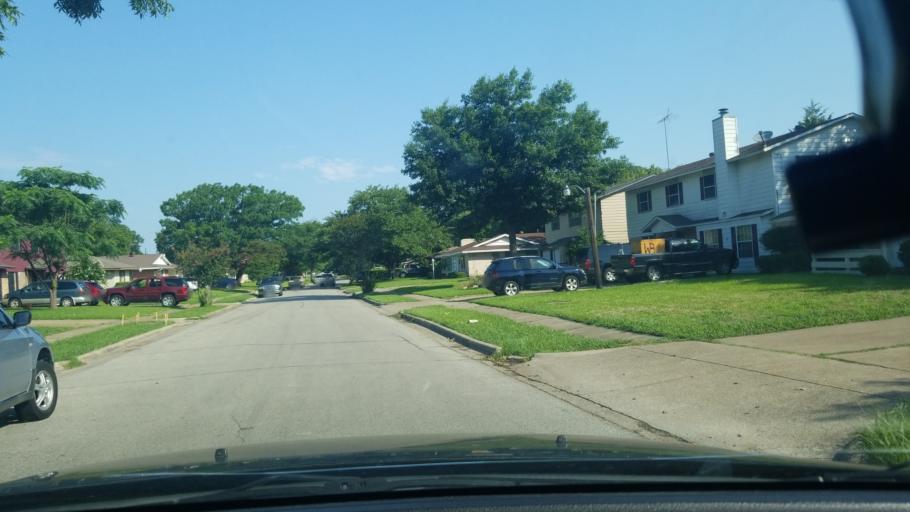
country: US
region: Texas
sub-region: Dallas County
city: Mesquite
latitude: 32.8243
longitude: -96.6383
